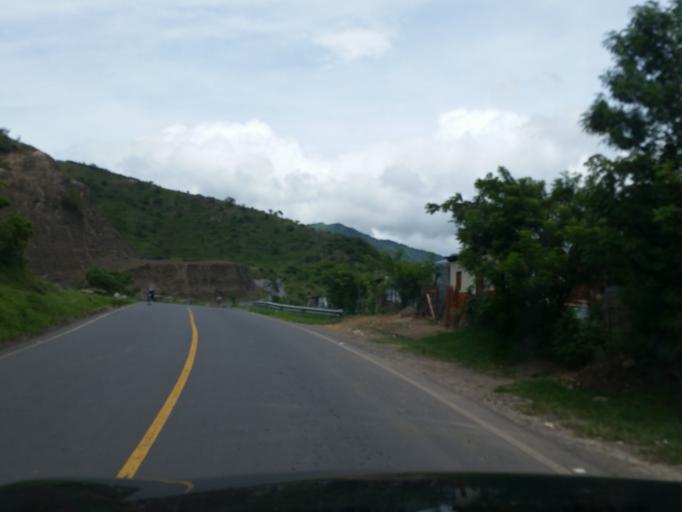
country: NI
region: Matagalpa
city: Matagalpa
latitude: 12.9473
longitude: -85.9203
